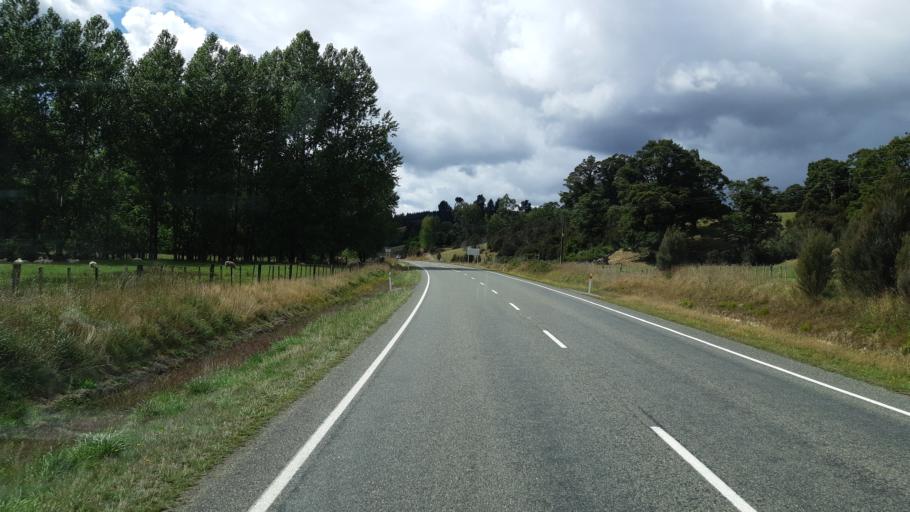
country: NZ
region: Tasman
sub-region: Tasman District
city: Wakefield
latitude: -41.6415
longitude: 172.6738
